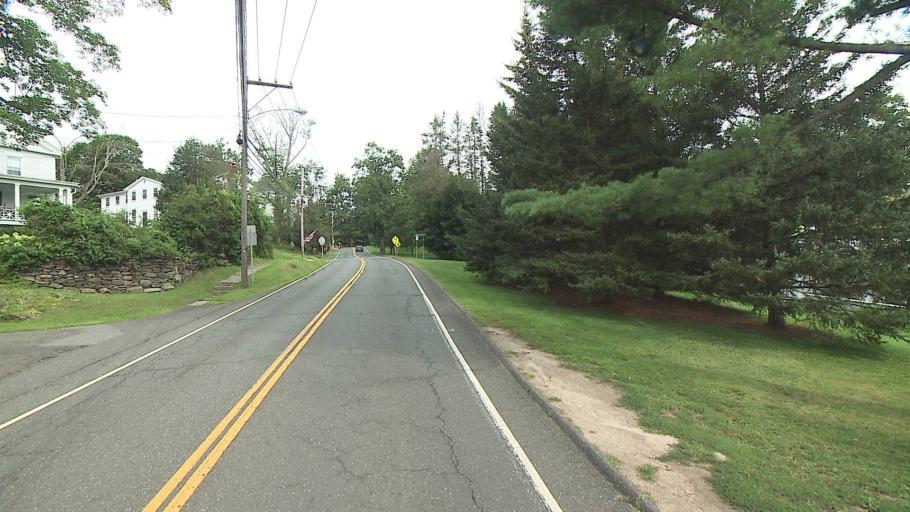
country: US
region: Connecticut
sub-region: Litchfield County
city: New Preston
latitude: 41.6295
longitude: -73.3105
